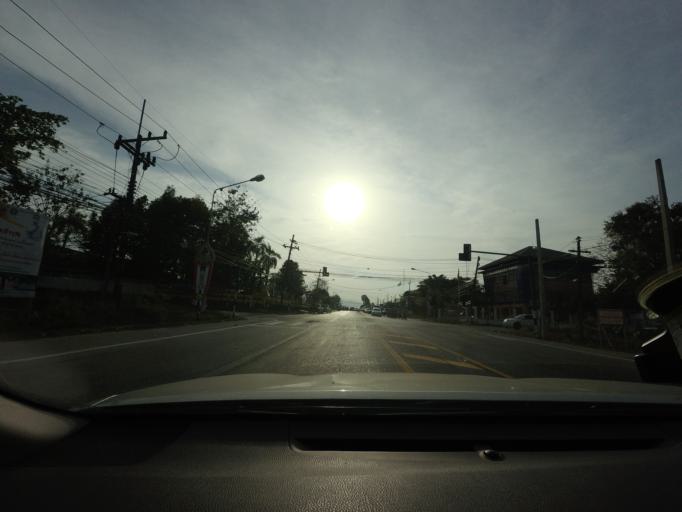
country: TH
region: Narathiwat
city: Ra-ngae
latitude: 6.2973
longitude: 101.7293
